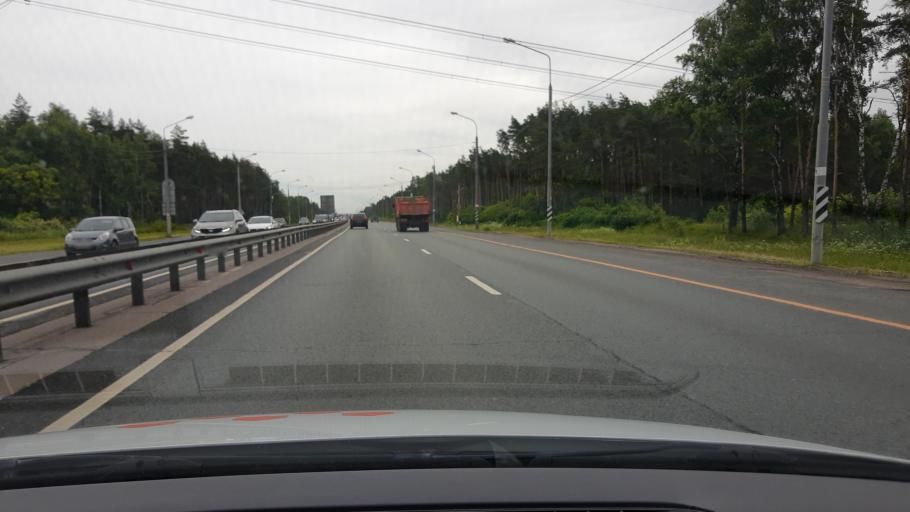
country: RU
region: Moskovskaya
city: Obukhovo
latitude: 55.8296
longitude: 38.2964
